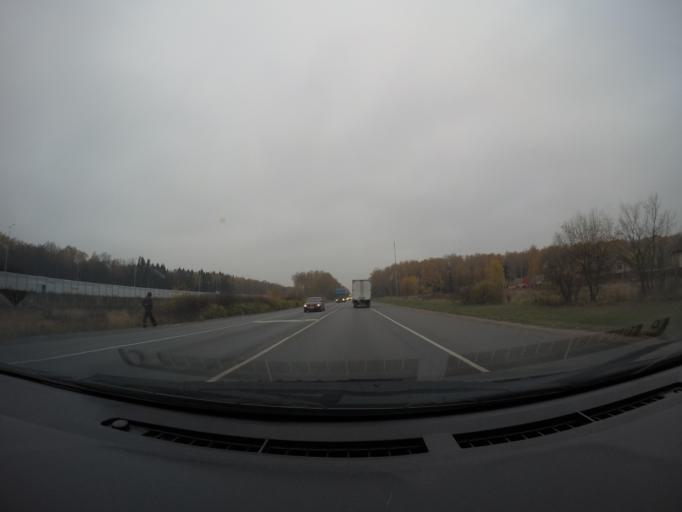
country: RU
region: Moskovskaya
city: Zhitnevo
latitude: 55.3506
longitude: 37.8932
